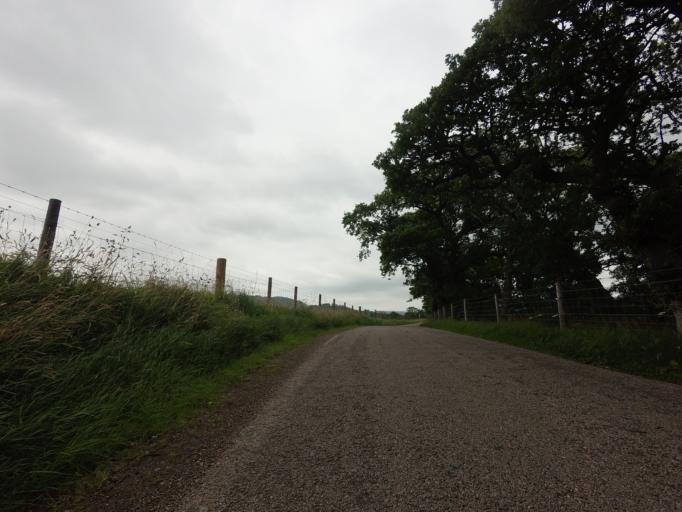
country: GB
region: Scotland
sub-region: Highland
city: Evanton
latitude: 57.9128
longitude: -4.3989
